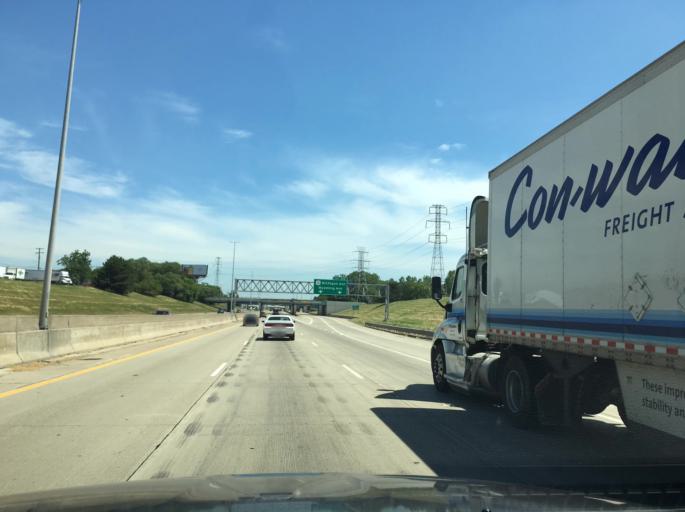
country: US
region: Michigan
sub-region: Wayne County
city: Dearborn
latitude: 42.3185
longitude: -83.1669
